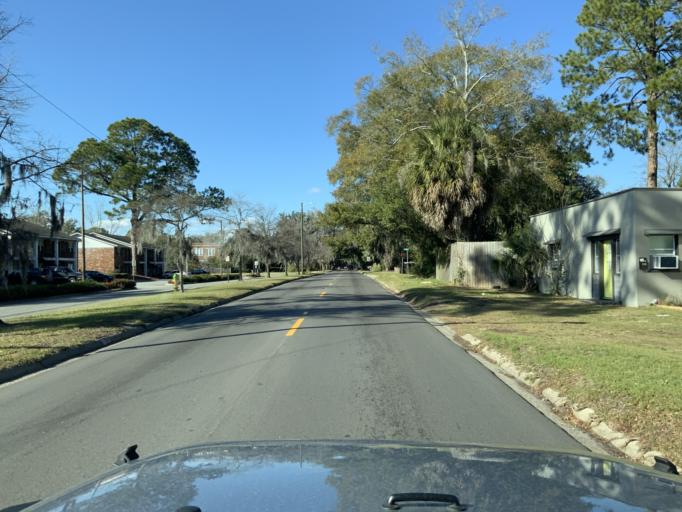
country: US
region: Georgia
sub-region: Chatham County
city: Thunderbolt
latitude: 32.0518
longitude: -81.0663
